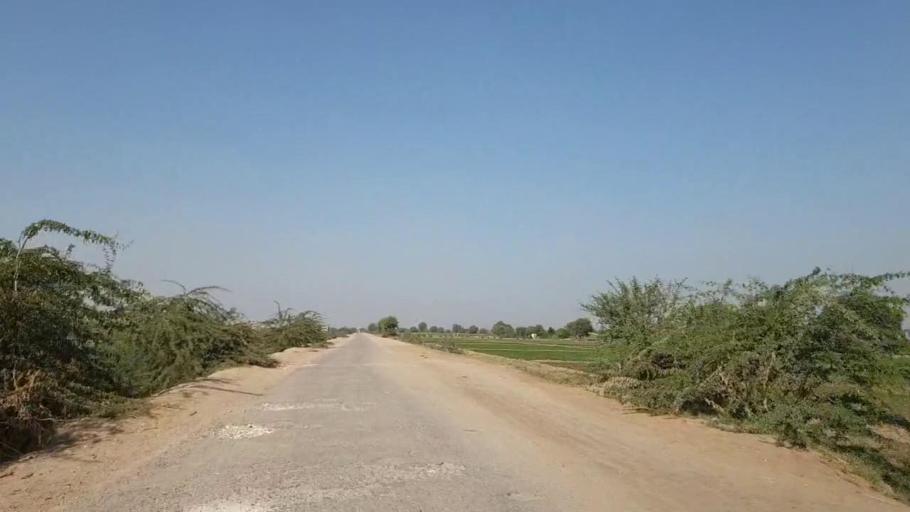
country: PK
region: Sindh
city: Digri
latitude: 25.0099
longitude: 69.1062
